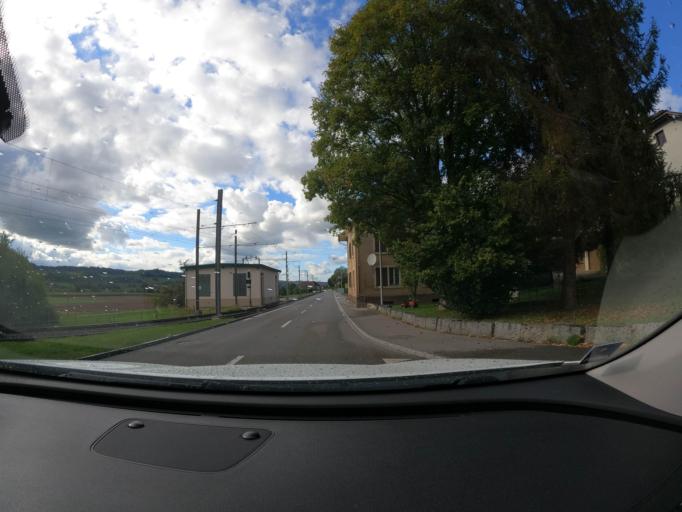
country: CH
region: Aargau
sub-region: Bezirk Kulm
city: Gontenschwil
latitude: 47.2735
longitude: 8.1676
